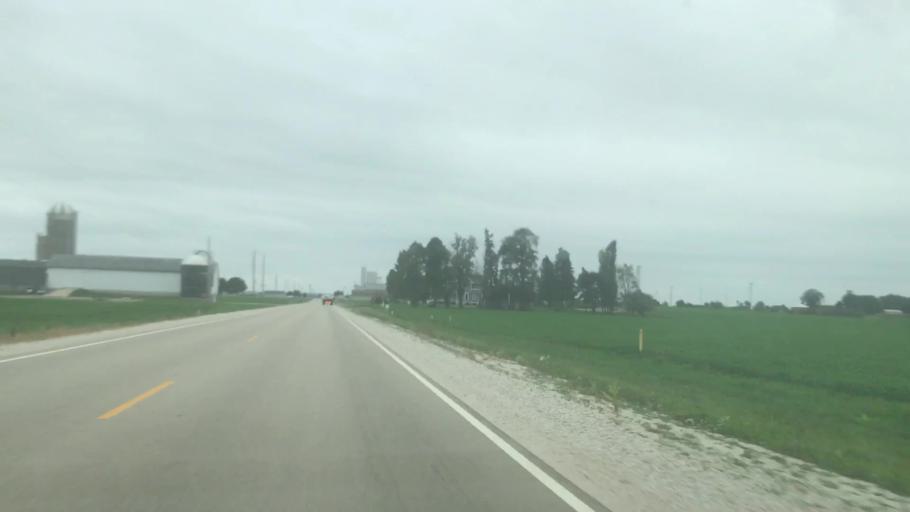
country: US
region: Wisconsin
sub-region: Fond du Lac County
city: Oakfield
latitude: 43.6226
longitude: -88.5417
